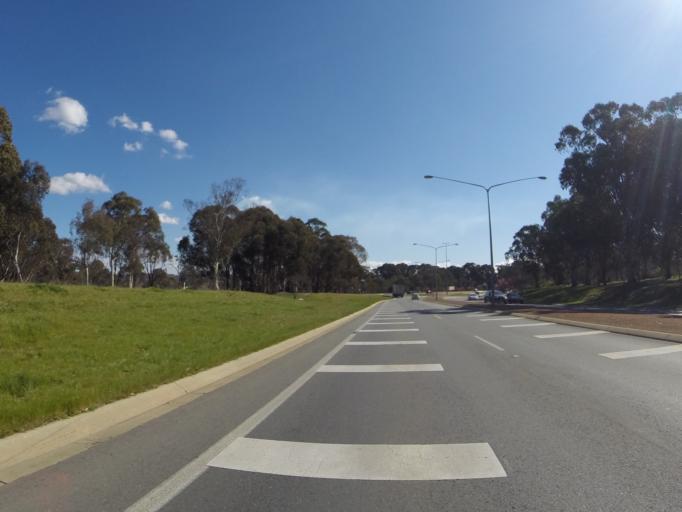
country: AU
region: Australian Capital Territory
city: Forrest
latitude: -35.3023
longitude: 149.1538
